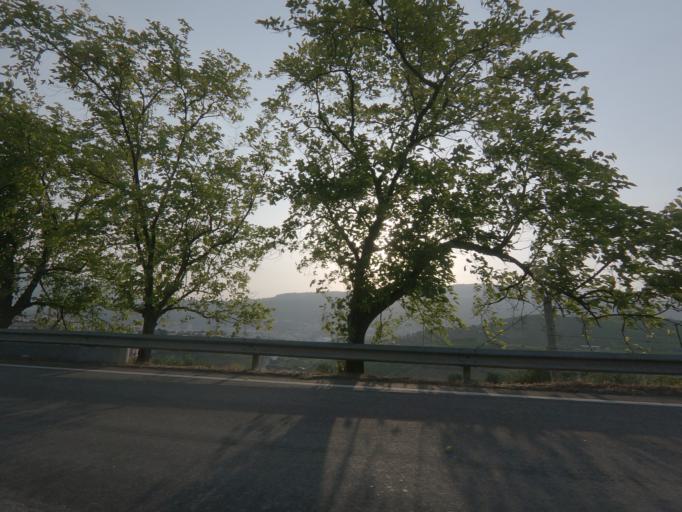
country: PT
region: Vila Real
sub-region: Peso da Regua
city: Peso da Regua
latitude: 41.1679
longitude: -7.7793
